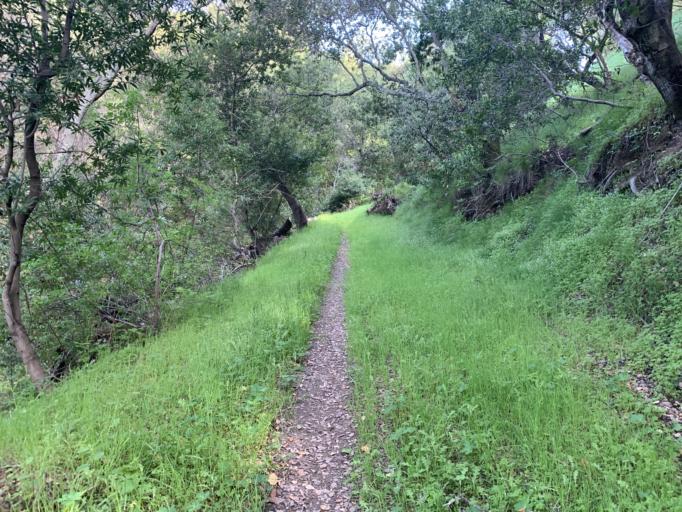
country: US
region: California
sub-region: Contra Costa County
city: Martinez
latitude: 38.0121
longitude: -122.1454
